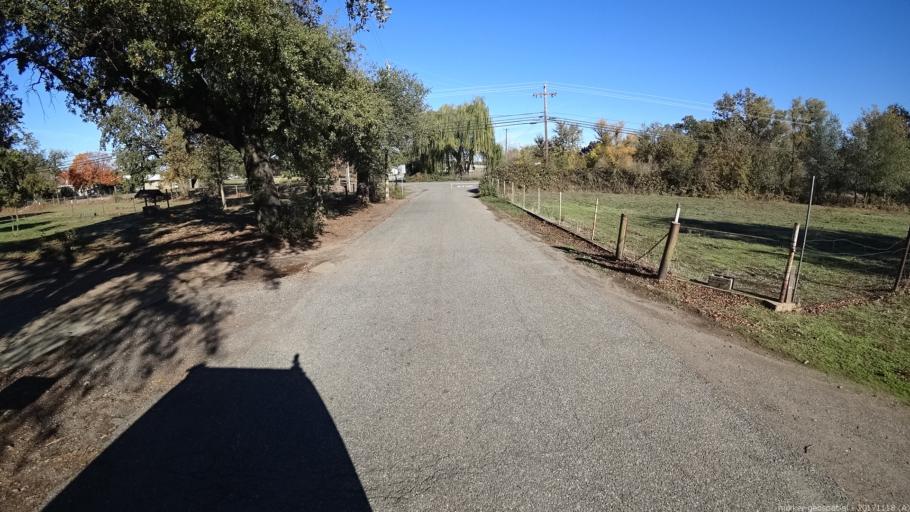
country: US
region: California
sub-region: Shasta County
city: Cottonwood
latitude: 40.3852
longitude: -122.3072
